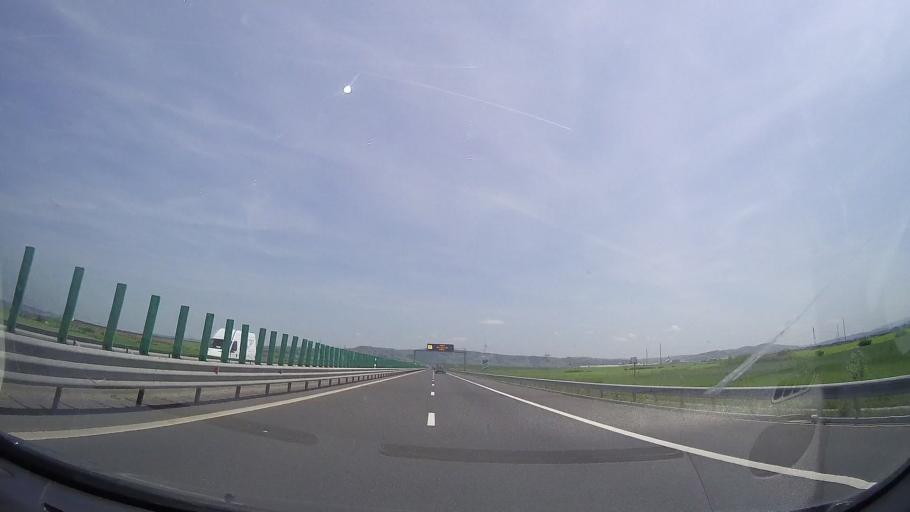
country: RO
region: Alba
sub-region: Comuna Pianu
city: Pianu de Jos
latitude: 45.9744
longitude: 23.5095
